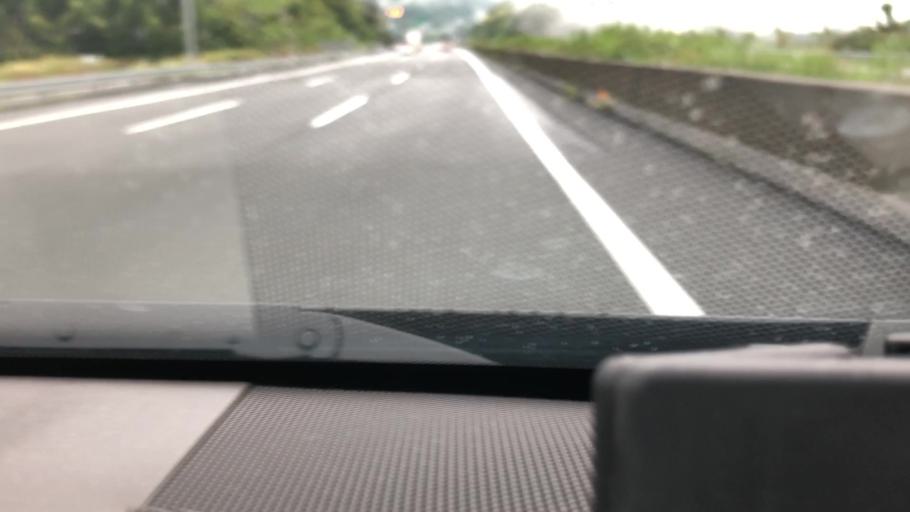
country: JP
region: Shizuoka
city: Shizuoka-shi
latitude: 34.9713
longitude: 138.2926
